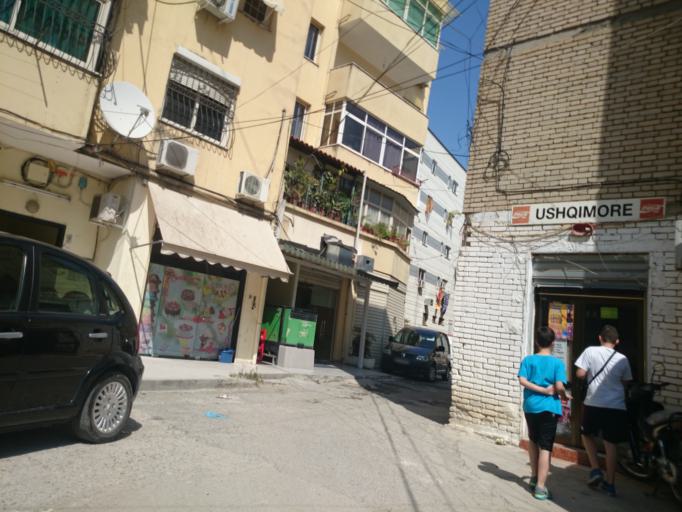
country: AL
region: Tirane
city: Tirana
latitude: 41.3255
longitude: 19.8310
